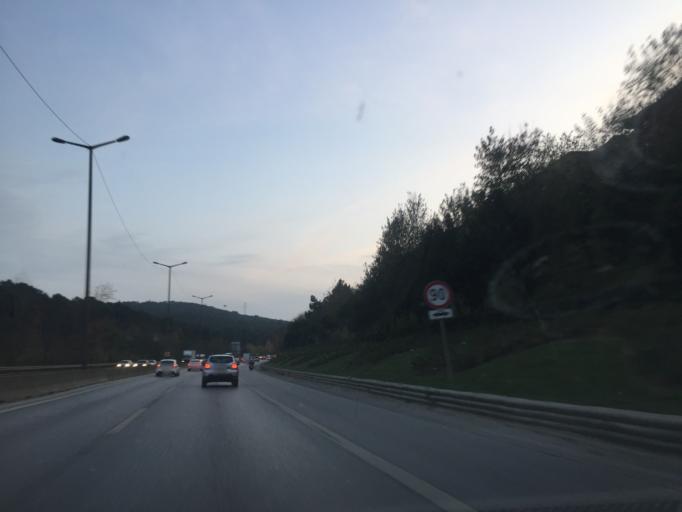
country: TR
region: Istanbul
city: Samandira
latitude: 40.9572
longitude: 29.2218
